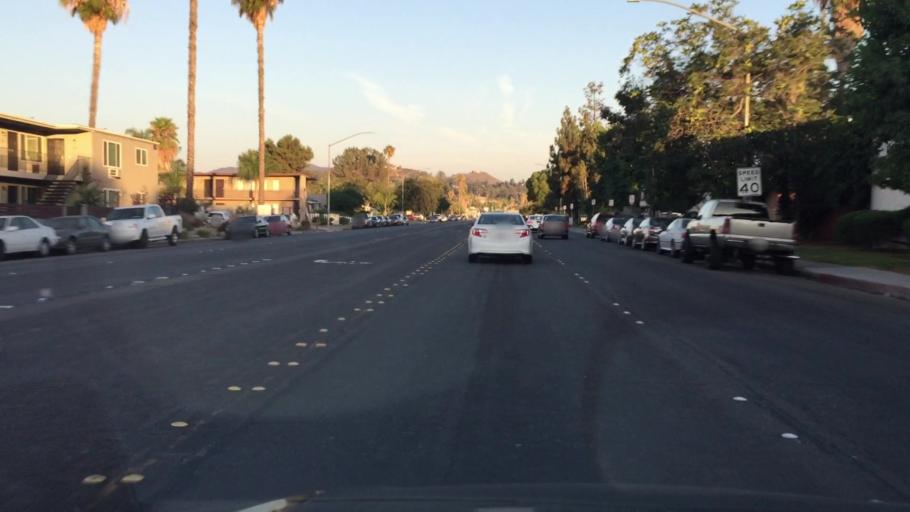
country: US
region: California
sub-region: San Diego County
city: Bostonia
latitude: 32.7917
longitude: -116.9327
